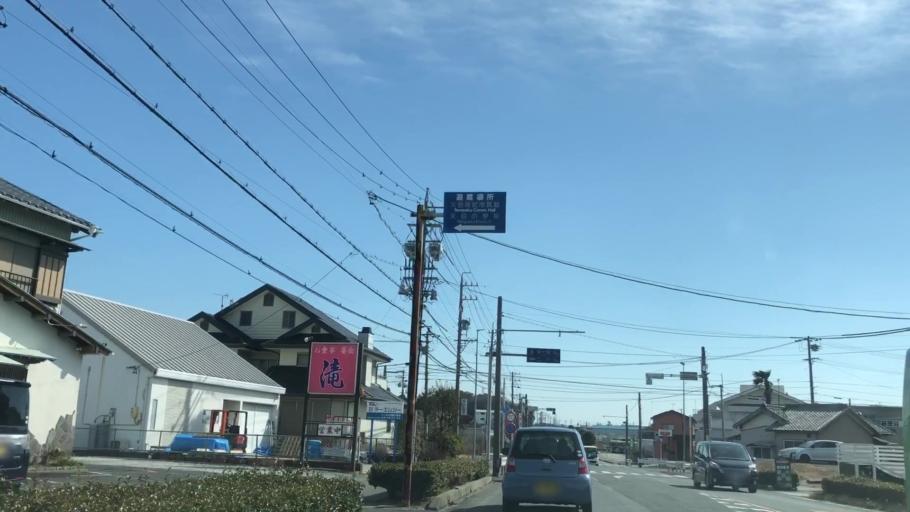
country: JP
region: Aichi
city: Toyohashi
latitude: 34.7076
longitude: 137.4106
